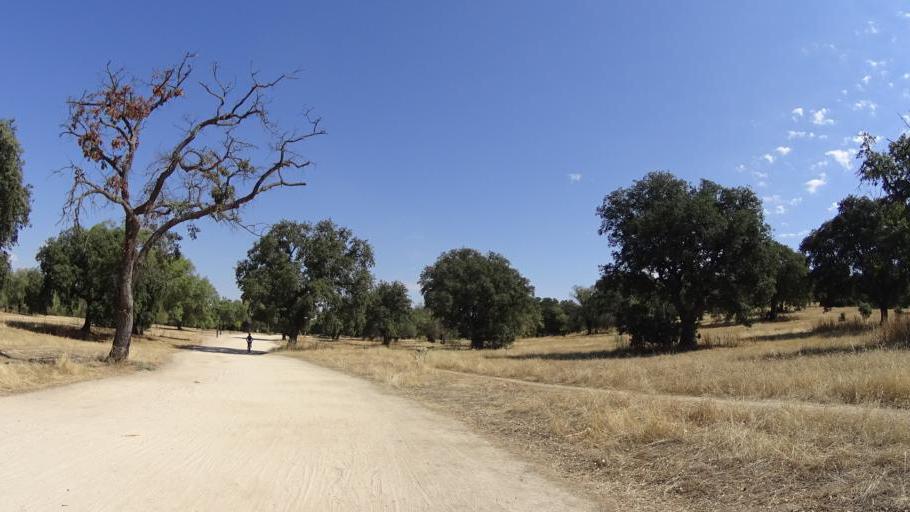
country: ES
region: Madrid
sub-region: Provincia de Madrid
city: Boadilla del Monte
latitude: 40.4119
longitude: -3.8653
